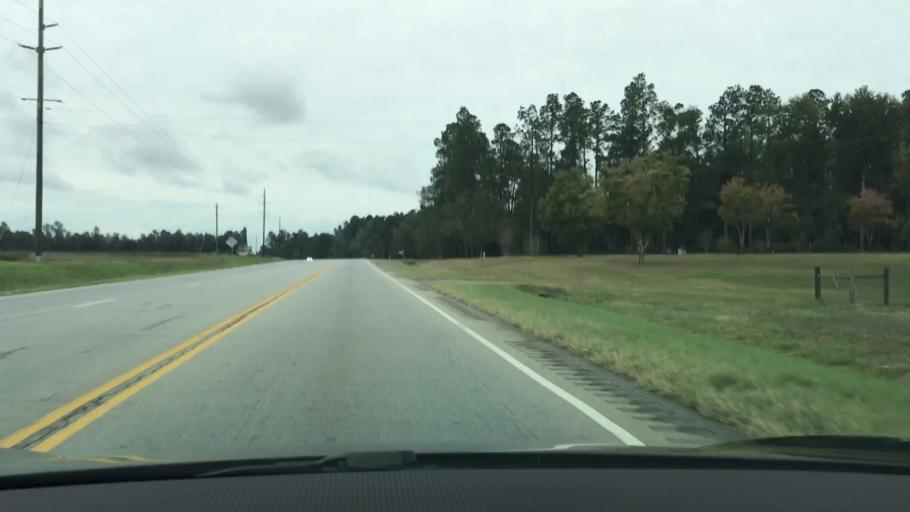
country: US
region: Georgia
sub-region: Jefferson County
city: Louisville
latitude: 33.0401
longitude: -82.4059
